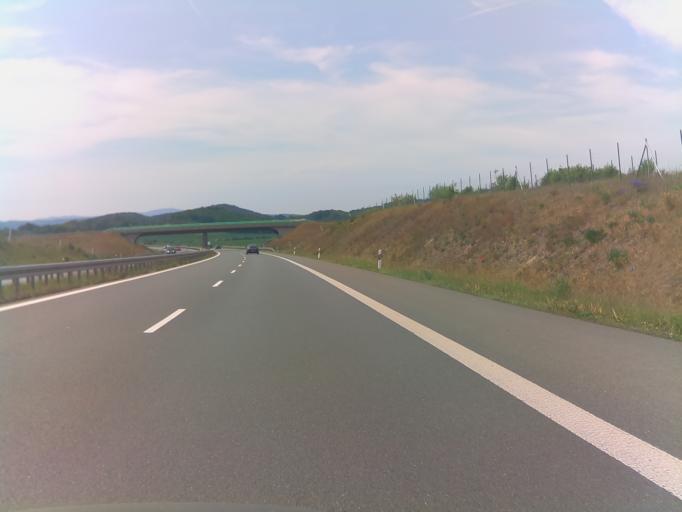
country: DE
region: Saxony-Anhalt
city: Westerhausen
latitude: 51.8178
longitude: 11.0699
